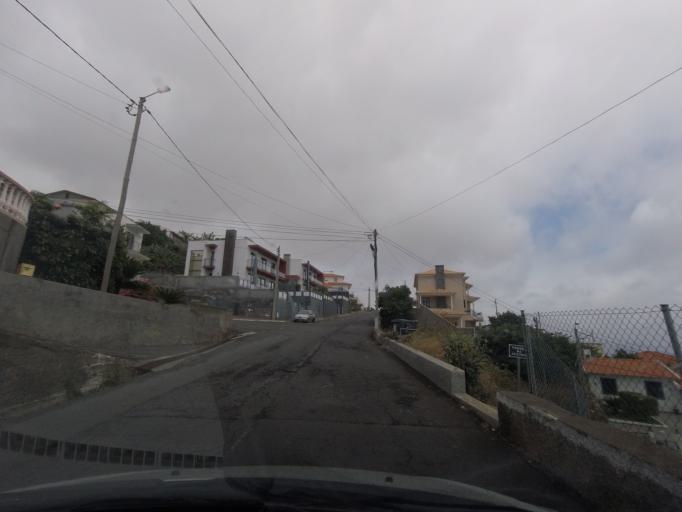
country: PT
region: Madeira
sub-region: Machico
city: Machico
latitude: 32.7034
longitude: -16.7765
